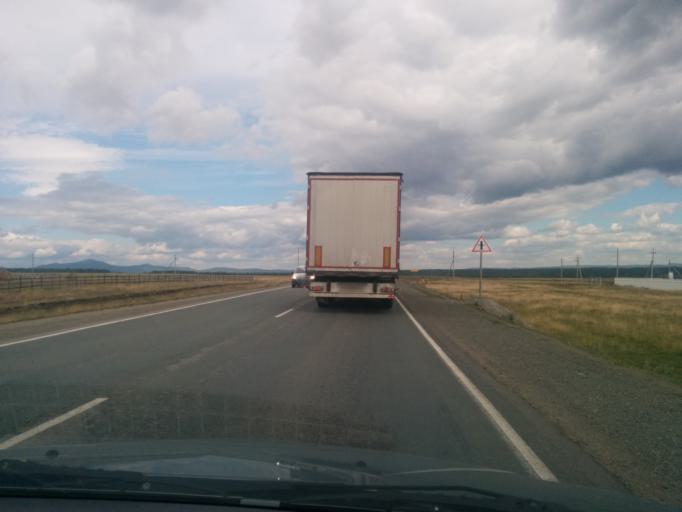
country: RU
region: Bashkortostan
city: Lomovka
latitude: 53.8813
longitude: 58.1134
